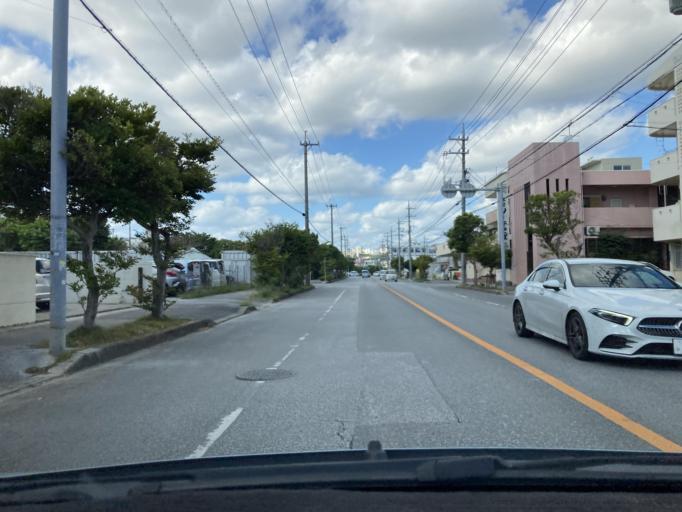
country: JP
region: Okinawa
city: Okinawa
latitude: 26.3206
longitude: 127.8342
